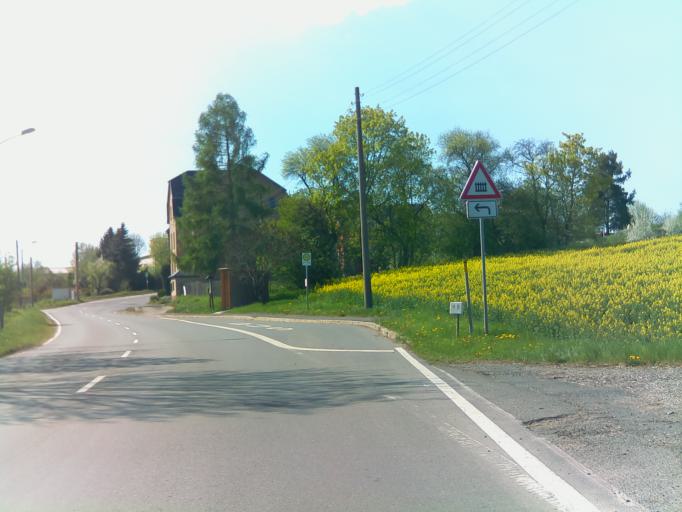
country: DE
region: Thuringia
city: Zeulenroda
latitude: 50.6277
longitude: 12.0280
